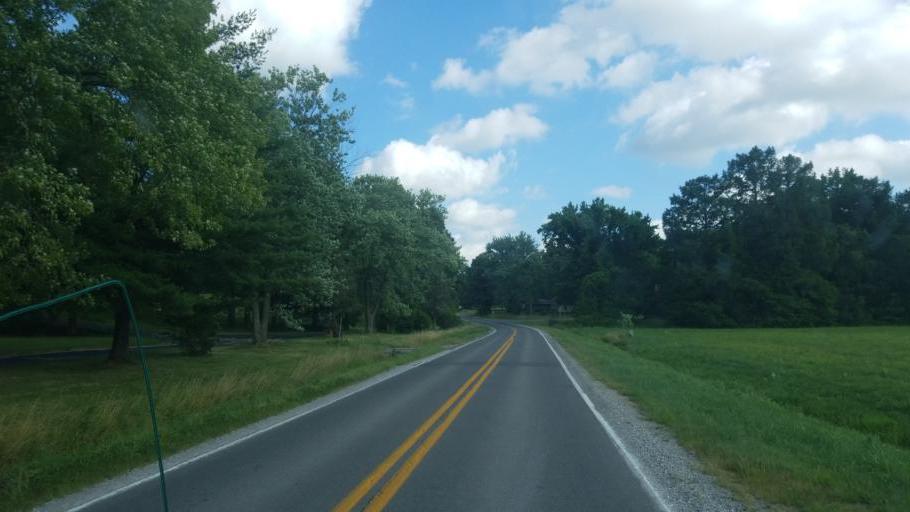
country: US
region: Illinois
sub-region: Union County
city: Cobden
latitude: 37.5463
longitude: -89.2661
